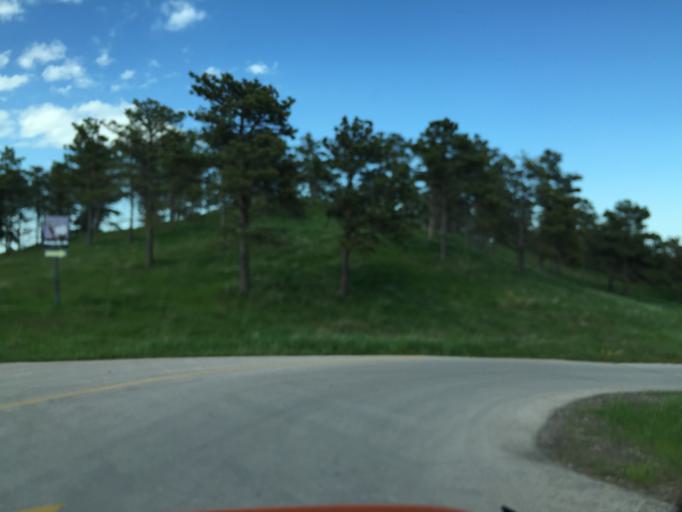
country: US
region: South Dakota
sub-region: Pennington County
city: Colonial Pine Hills
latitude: 43.9763
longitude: -103.2970
